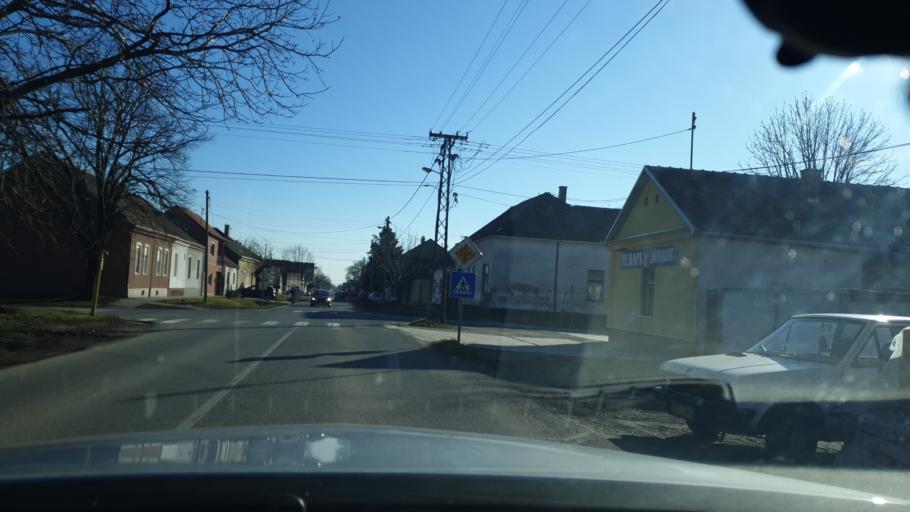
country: RS
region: Autonomna Pokrajina Vojvodina
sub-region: Sremski Okrug
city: Ruma
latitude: 45.0107
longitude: 19.8161
